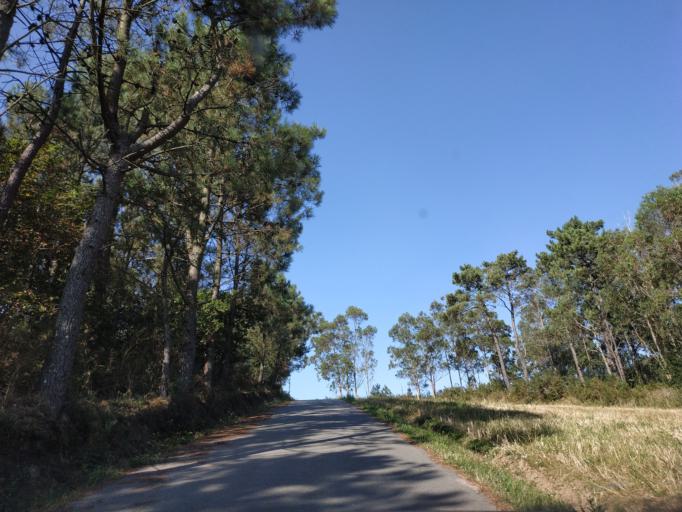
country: ES
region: Galicia
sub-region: Provincia da Coruna
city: Laracha
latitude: 43.2288
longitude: -8.5351
